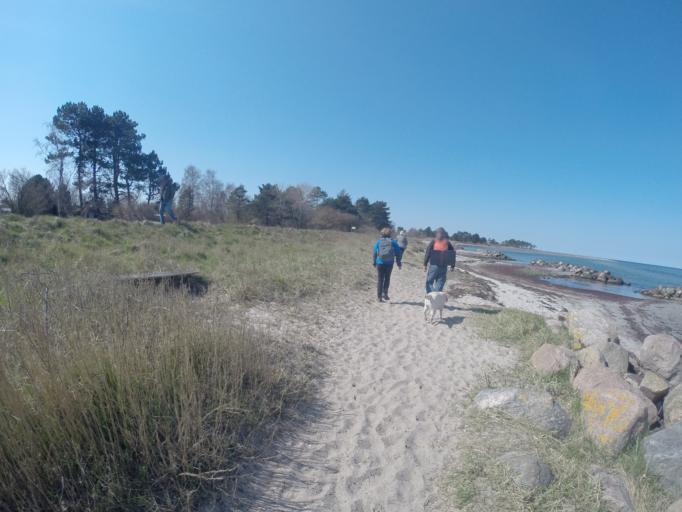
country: DK
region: Zealand
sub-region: Kalundborg Kommune
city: Gorlev
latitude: 55.5335
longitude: 11.1042
